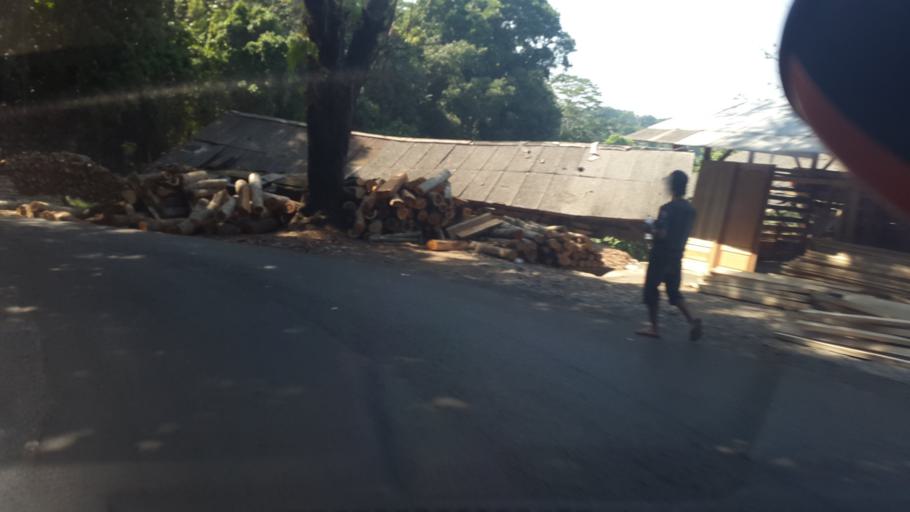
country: ID
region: West Java
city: Cicurug
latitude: -6.8280
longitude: 106.7352
